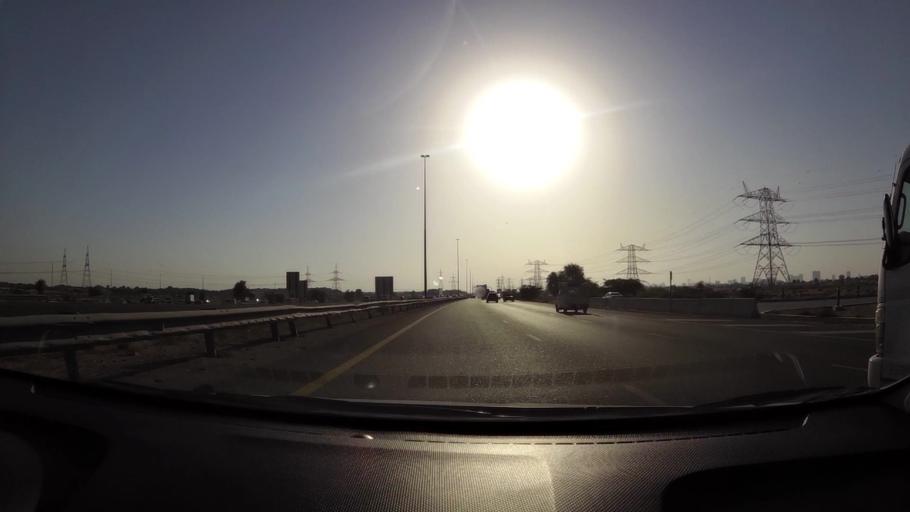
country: AE
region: Ajman
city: Ajman
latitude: 25.3572
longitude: 55.5009
